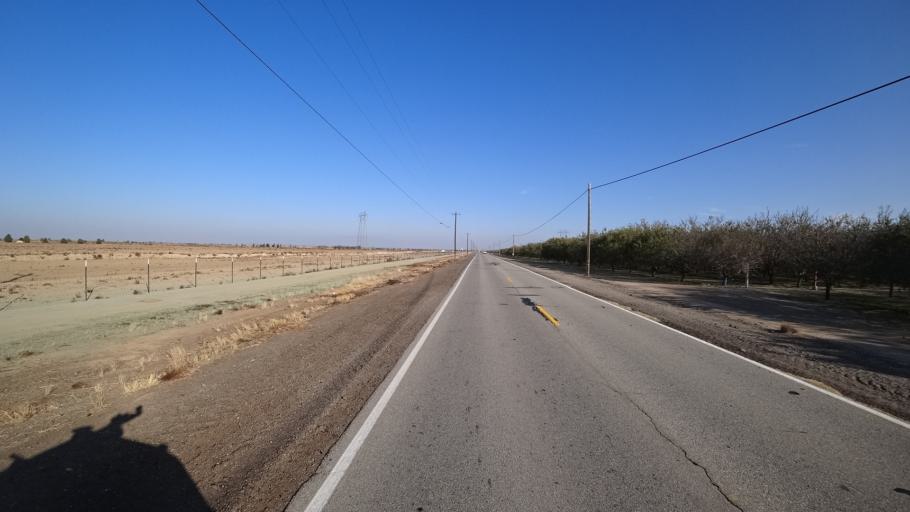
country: US
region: California
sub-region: Kern County
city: Rosedale
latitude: 35.2962
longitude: -119.1778
